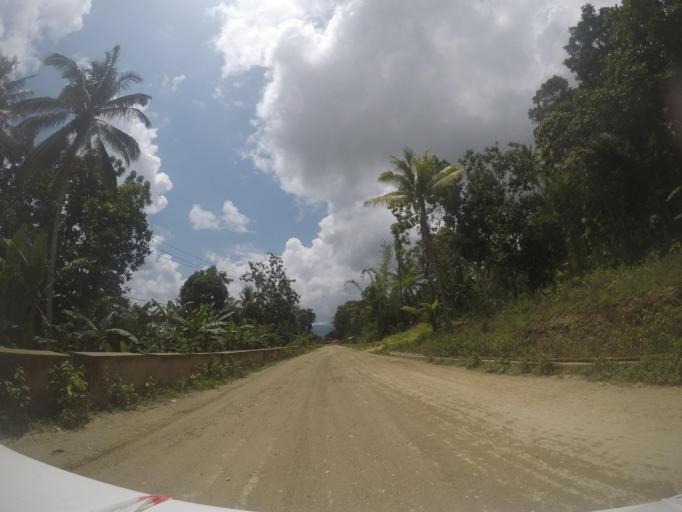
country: TL
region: Baucau
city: Venilale
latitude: -8.5889
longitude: 126.3869
